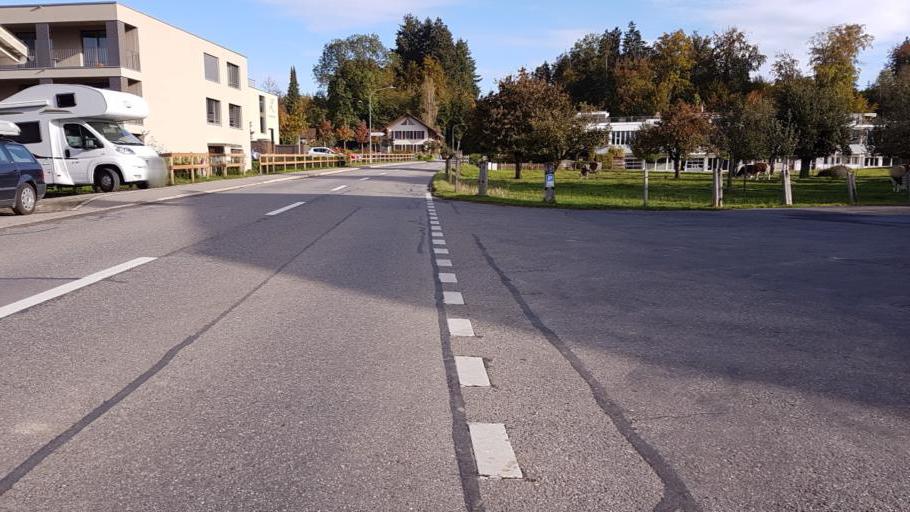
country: CH
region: Bern
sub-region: Bern-Mittelland District
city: Worb
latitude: 46.9114
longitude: 7.5590
